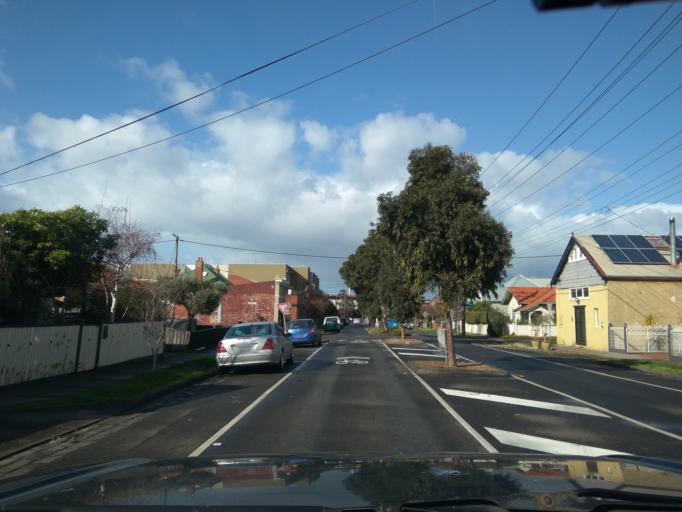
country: AU
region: Victoria
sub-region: Maribyrnong
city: Yarraville
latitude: -37.8195
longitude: 144.8938
